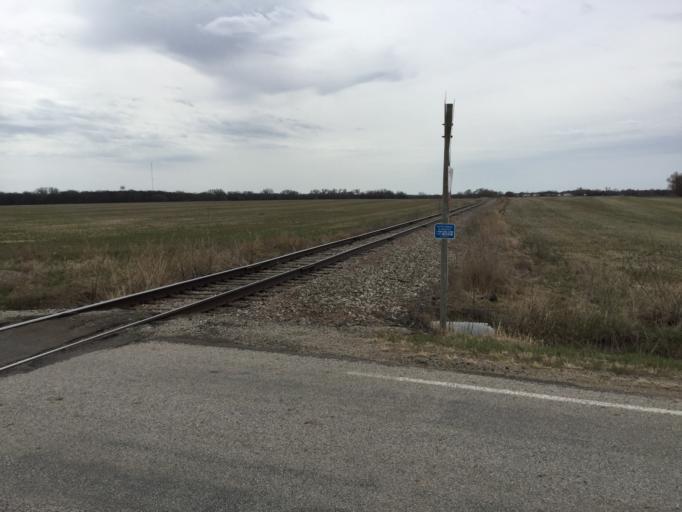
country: US
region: Kansas
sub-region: Ottawa County
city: Minneapolis
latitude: 39.1467
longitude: -97.7240
